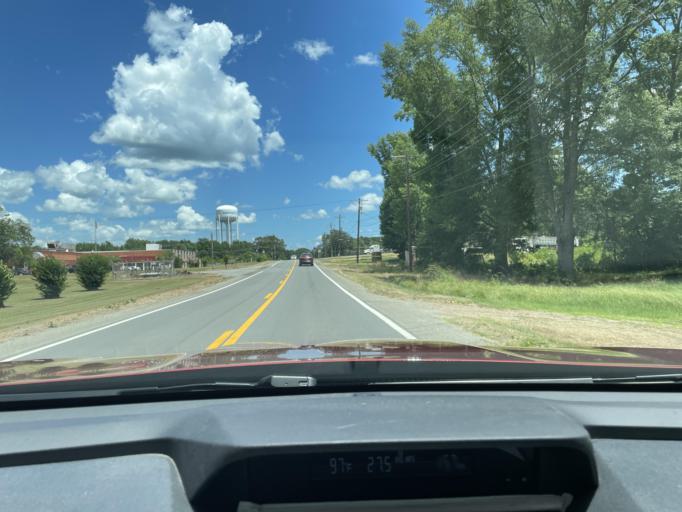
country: US
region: Arkansas
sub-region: Drew County
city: Monticello
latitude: 33.6283
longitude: -91.7714
